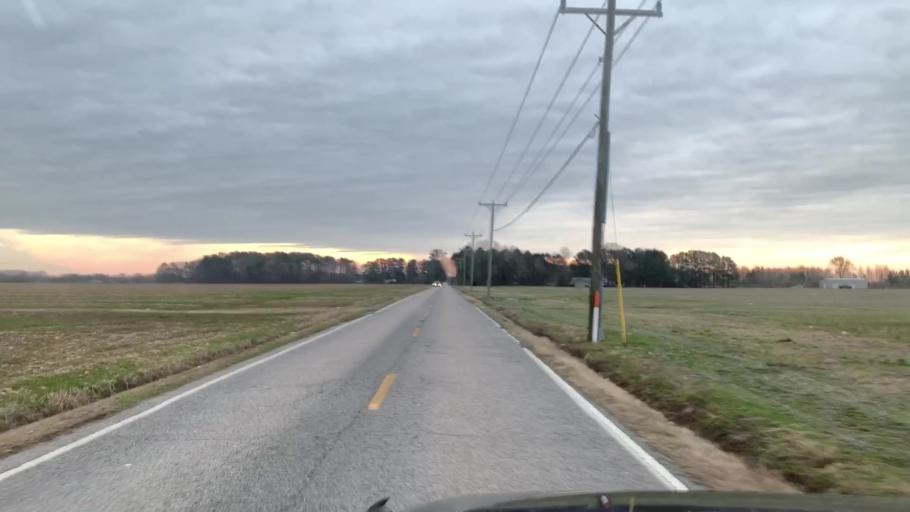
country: US
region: North Carolina
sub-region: Currituck County
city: Moyock
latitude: 36.6337
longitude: -76.1851
